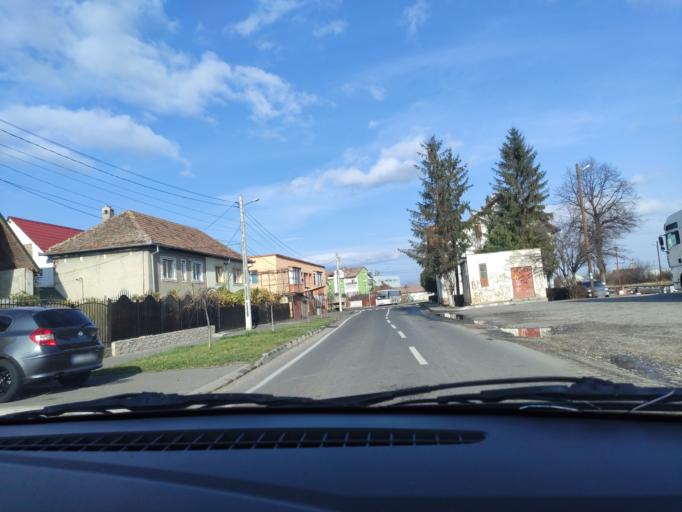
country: RO
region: Brasov
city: Codlea
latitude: 45.6929
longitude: 25.4568
